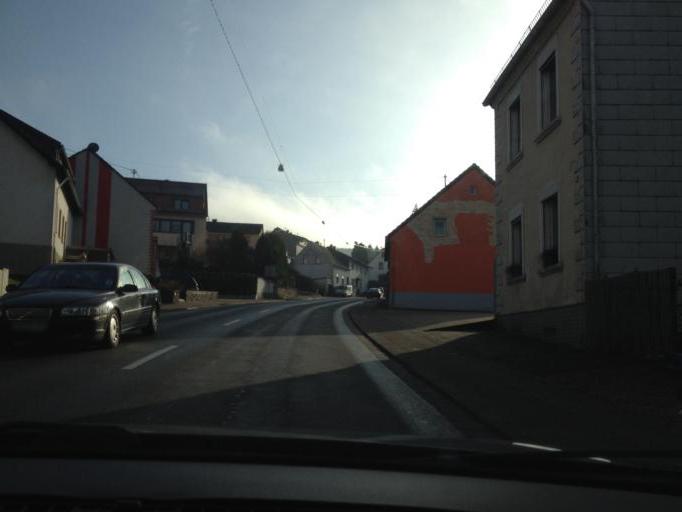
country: DE
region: Saarland
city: Marpingen
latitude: 49.4500
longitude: 7.0572
